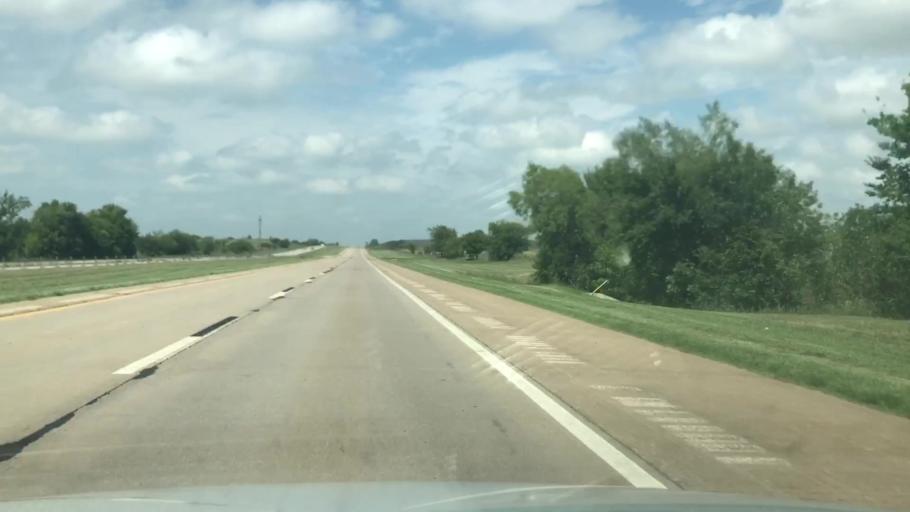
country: US
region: Oklahoma
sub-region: Osage County
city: Skiatook
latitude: 36.3996
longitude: -95.9203
